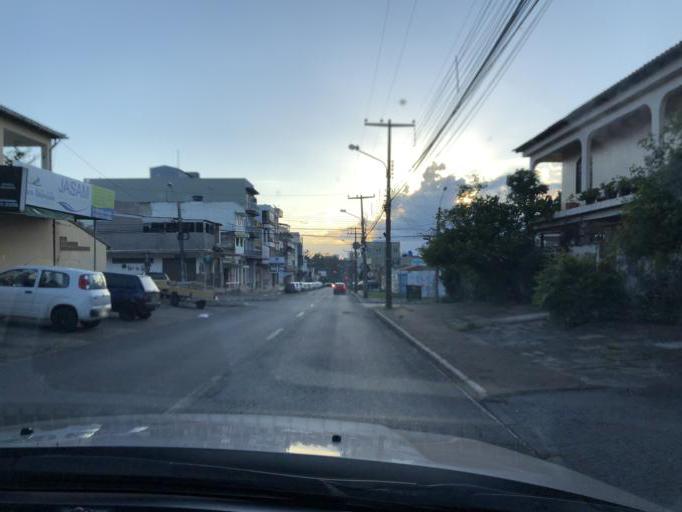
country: BR
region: Federal District
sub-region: Brasilia
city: Brasilia
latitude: -15.8468
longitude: -48.0466
